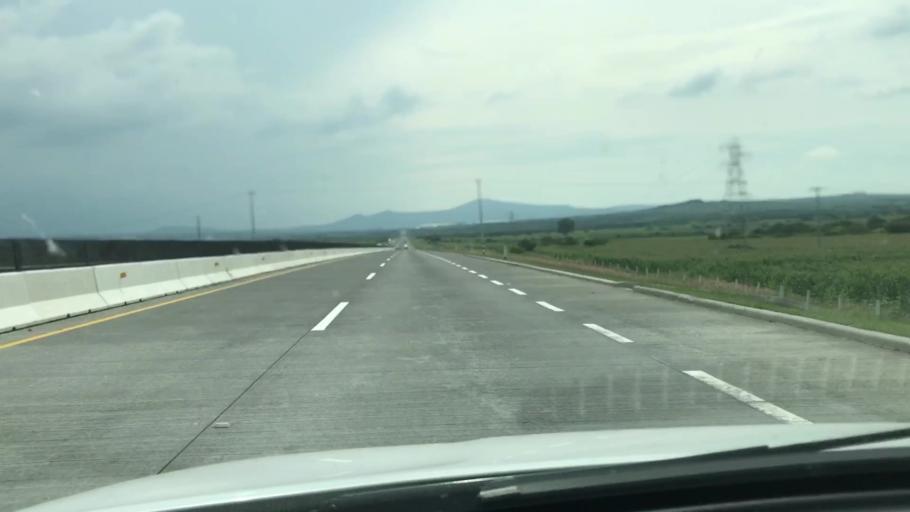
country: MX
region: Michoacan
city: La Piedad Cavadas
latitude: 20.3984
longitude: -102.0570
